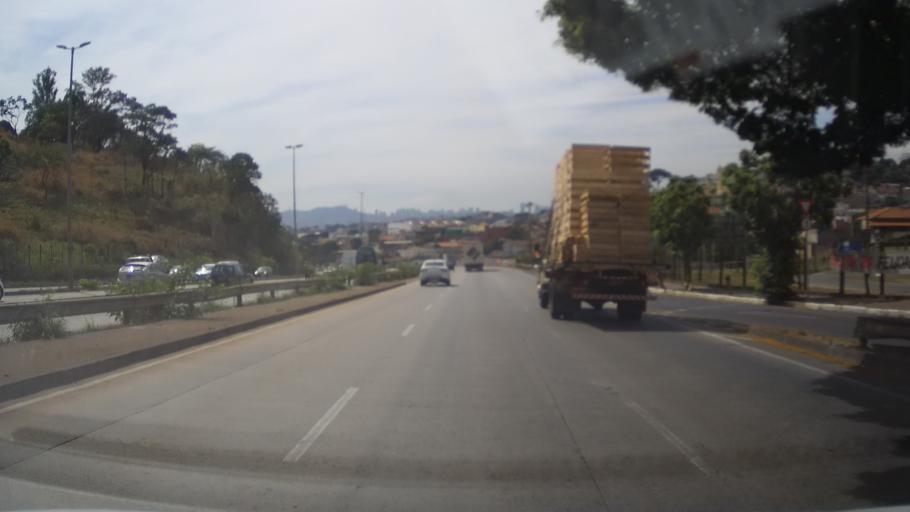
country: BR
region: Minas Gerais
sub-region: Contagem
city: Contagem
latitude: -19.9318
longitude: -44.0146
